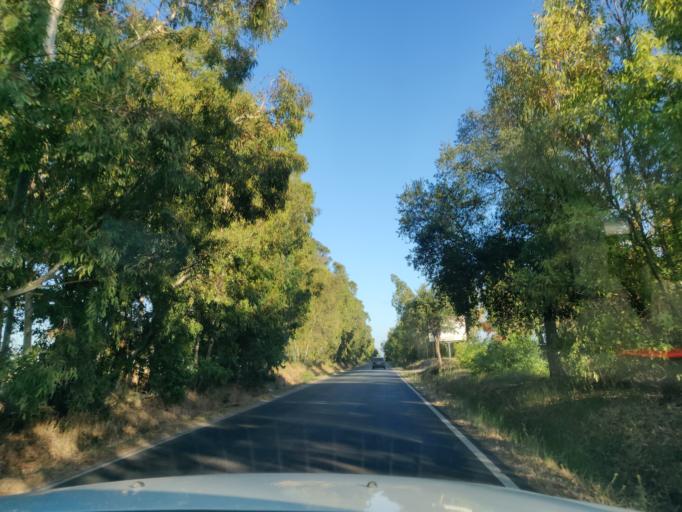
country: IT
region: Latium
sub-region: Provincia di Viterbo
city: Tarquinia
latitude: 42.2802
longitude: 11.6745
